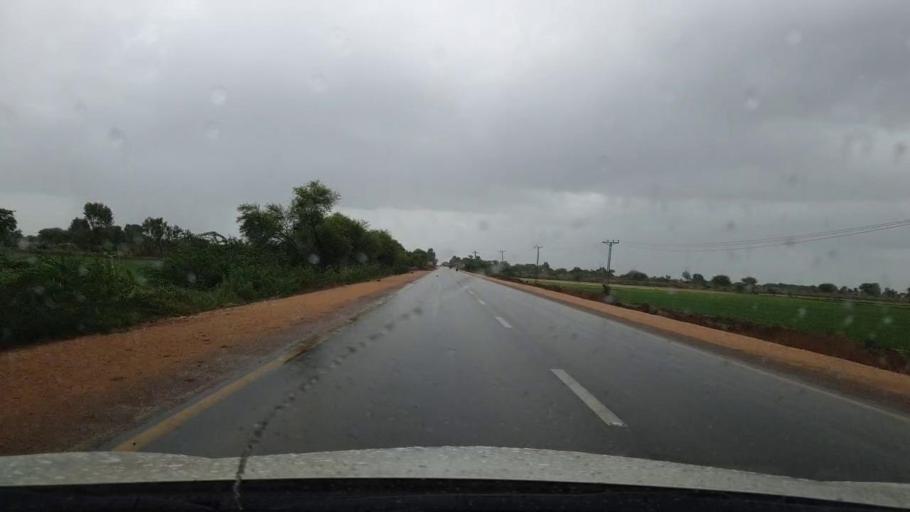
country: PK
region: Sindh
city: Kario
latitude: 24.6530
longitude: 68.5986
